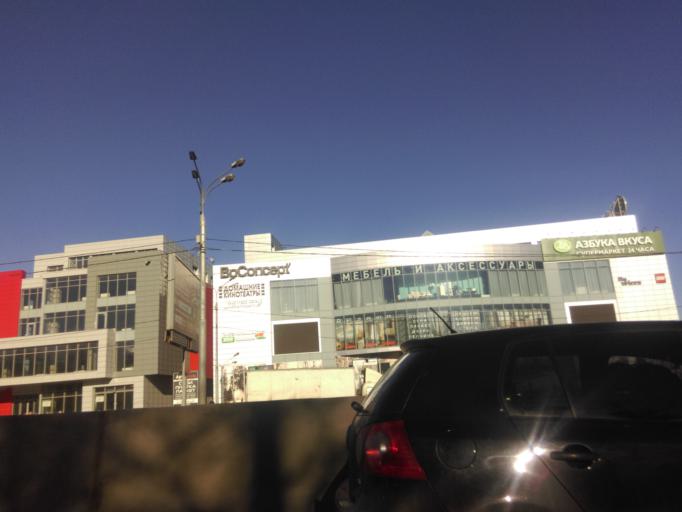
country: RU
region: Moskovskaya
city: Novoivanovskoye
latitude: 55.7083
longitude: 37.3623
